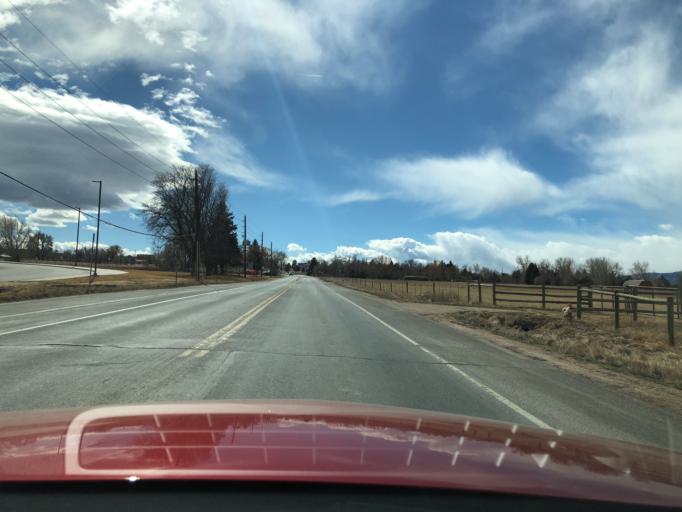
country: US
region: Colorado
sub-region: Boulder County
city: Superior
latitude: 40.0039
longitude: -105.1783
